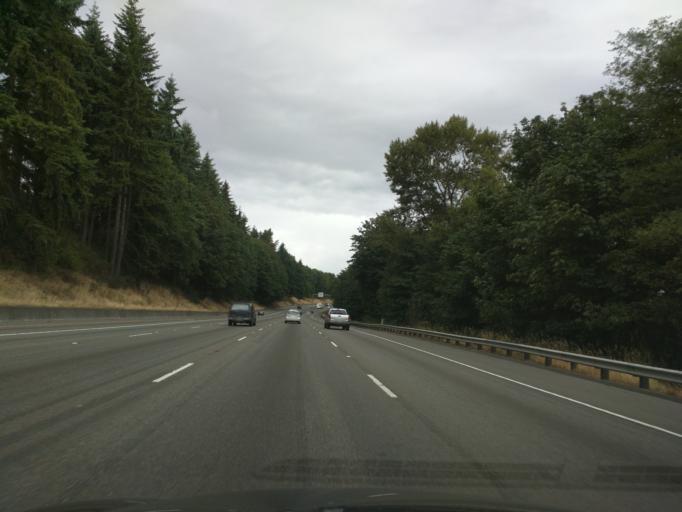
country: US
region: Washington
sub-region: Snohomish County
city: Everett
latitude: 47.9368
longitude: -122.1963
